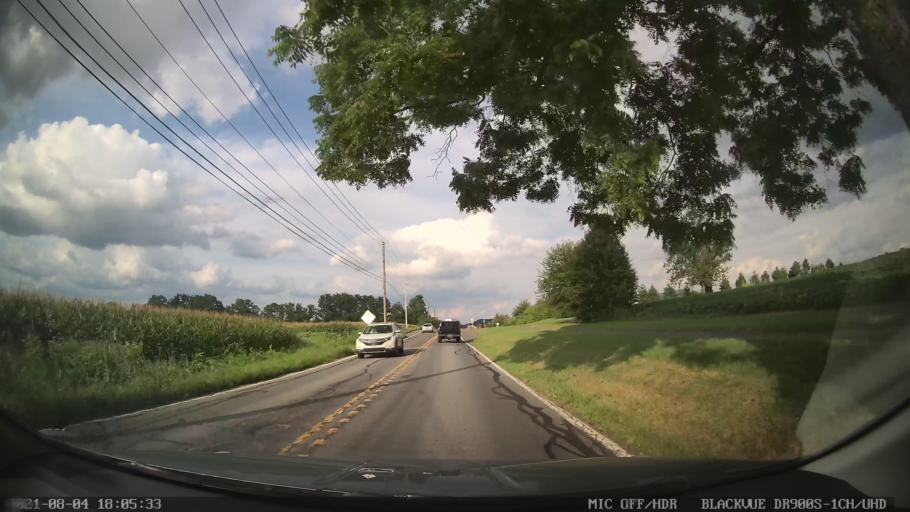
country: US
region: Pennsylvania
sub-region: Lehigh County
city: Ancient Oaks
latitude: 40.5617
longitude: -75.5947
